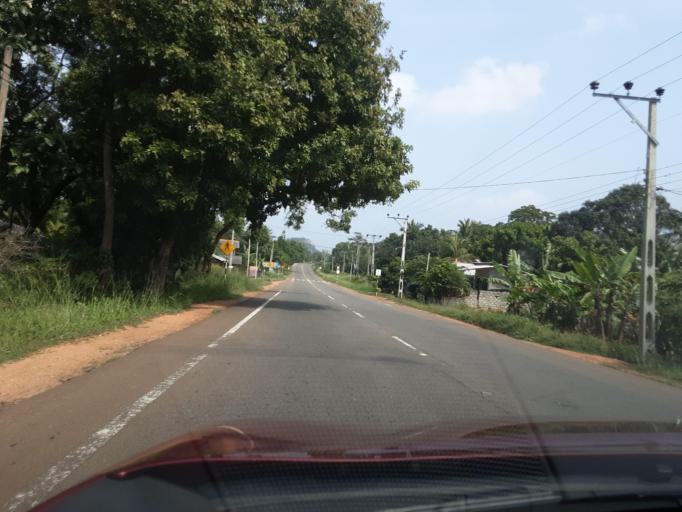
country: LK
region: North Central
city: Anuradhapura
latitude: 8.3364
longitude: 80.5016
